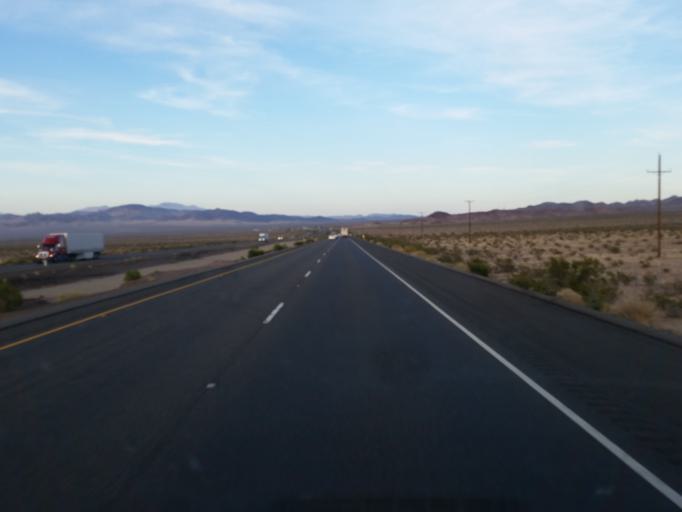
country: US
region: California
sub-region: San Bernardino County
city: Joshua Tree
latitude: 34.7249
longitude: -116.2153
